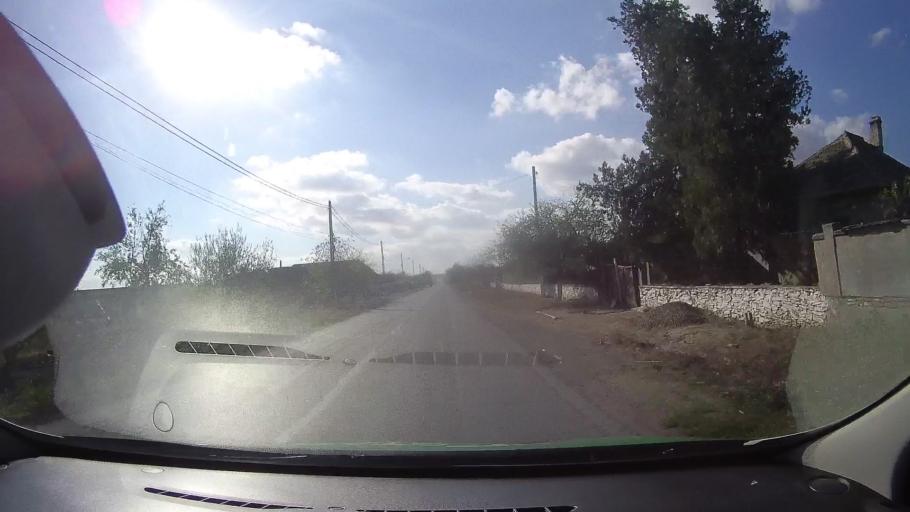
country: RO
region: Constanta
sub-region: Comuna Mihai Viteazu
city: Mihai Viteazu
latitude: 44.6255
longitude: 28.7316
